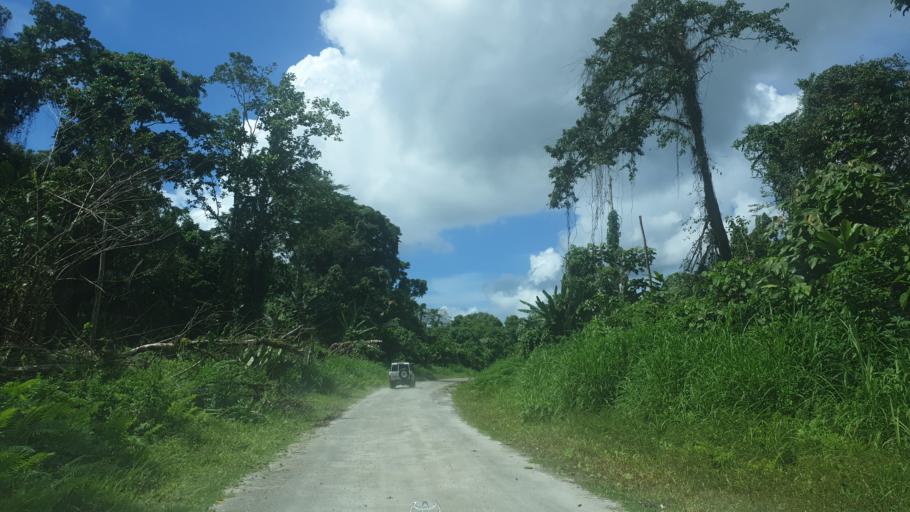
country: PG
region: Bougainville
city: Panguna
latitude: -6.7357
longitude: 155.4987
